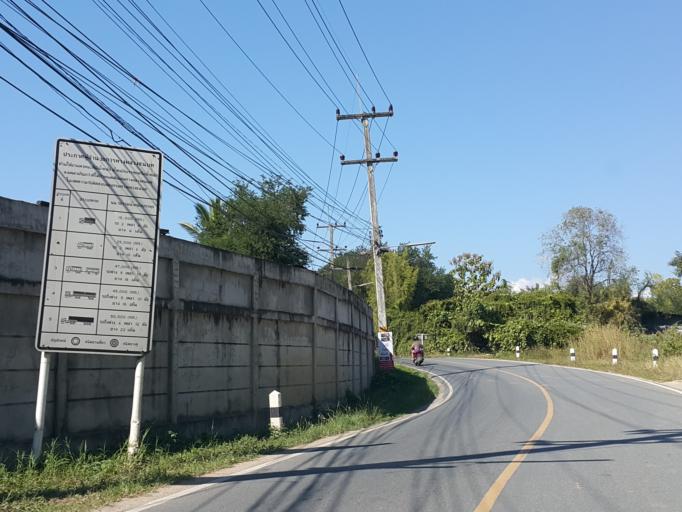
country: TH
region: Chiang Mai
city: San Sai
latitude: 18.9386
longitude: 98.9318
